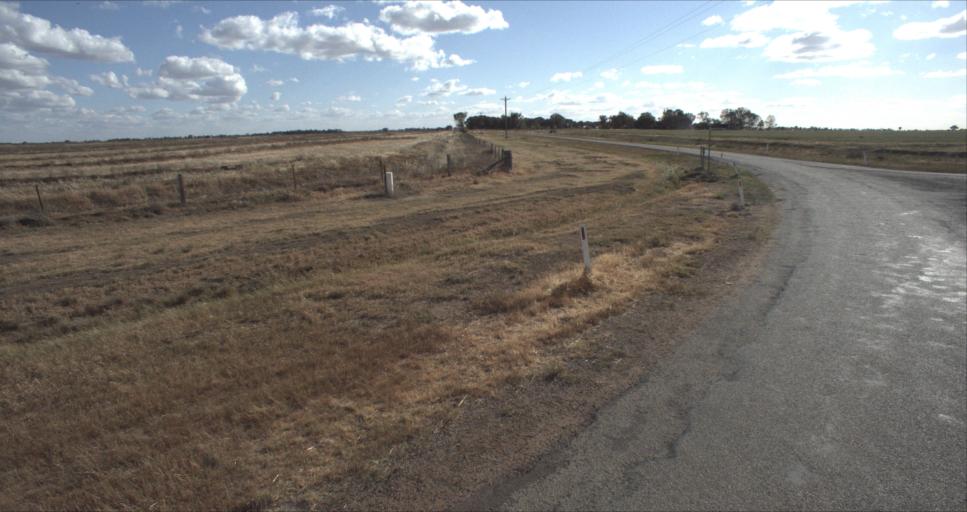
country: AU
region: New South Wales
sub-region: Leeton
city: Leeton
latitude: -34.4551
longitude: 146.2754
